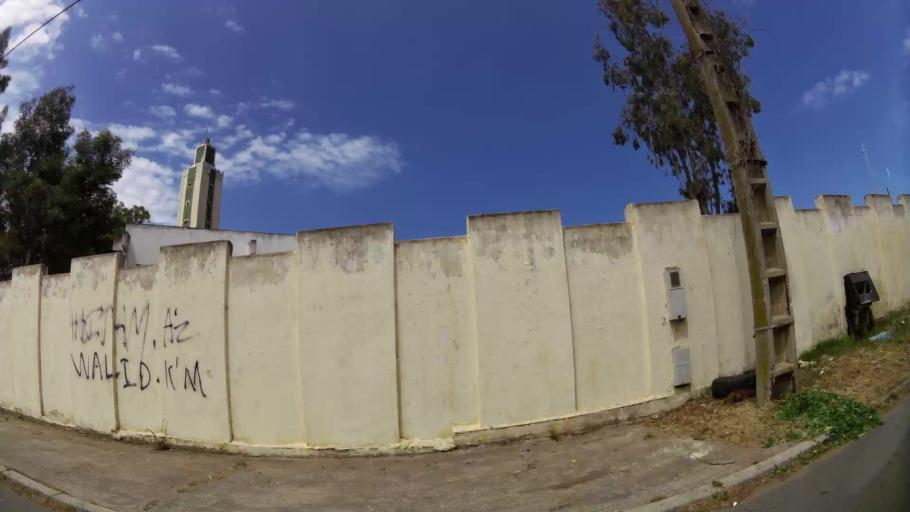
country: MA
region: Gharb-Chrarda-Beni Hssen
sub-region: Kenitra Province
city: Kenitra
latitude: 34.2558
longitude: -6.6024
